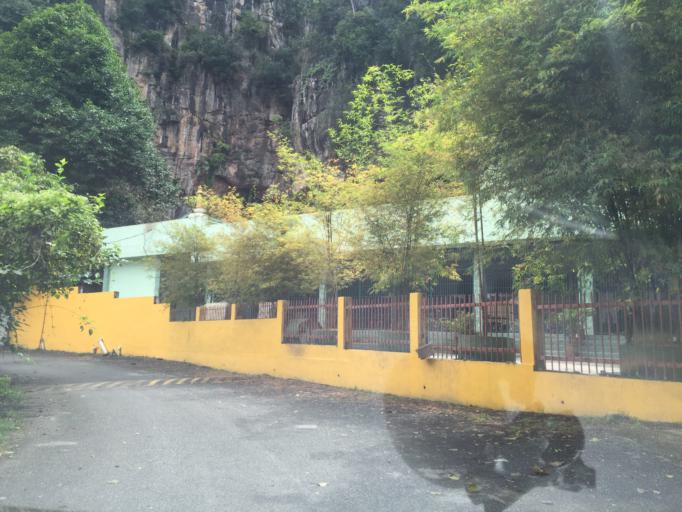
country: MY
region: Perak
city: Ipoh
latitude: 4.5617
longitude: 101.1248
